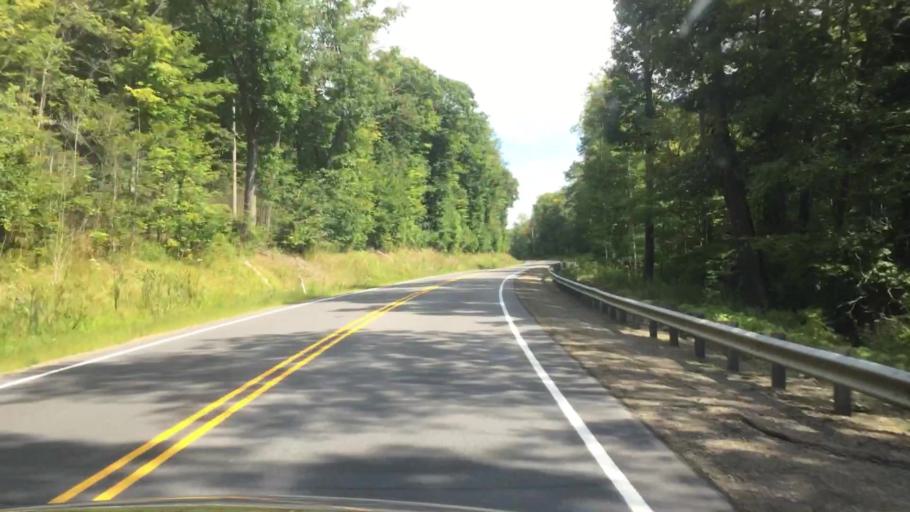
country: US
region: Pennsylvania
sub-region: McKean County
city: Bradford
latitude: 41.8859
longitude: -78.5911
